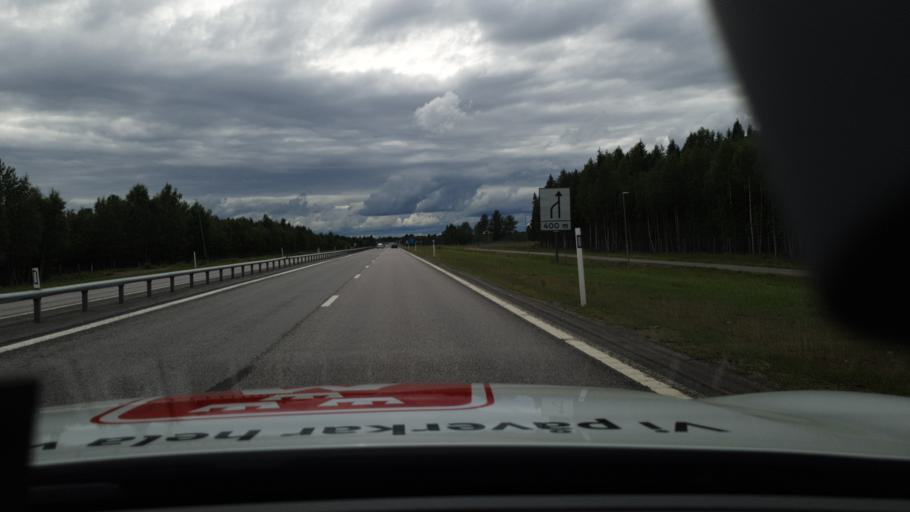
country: SE
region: Norrbotten
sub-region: Pitea Kommun
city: Rosvik
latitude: 65.5407
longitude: 21.8213
